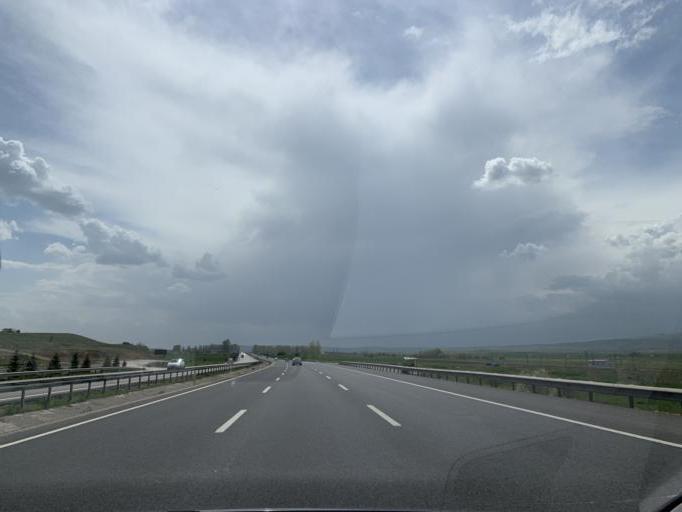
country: TR
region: Ankara
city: Temelli
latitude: 39.7013
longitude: 32.2699
